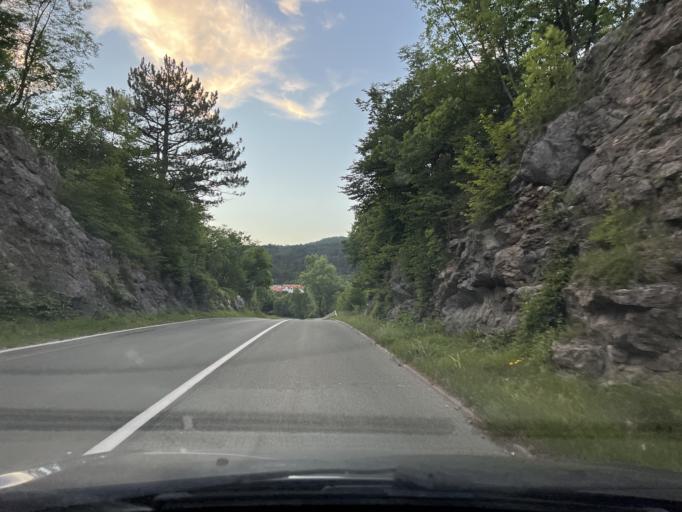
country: HR
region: Primorsko-Goranska
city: Klana
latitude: 45.4442
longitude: 14.3456
